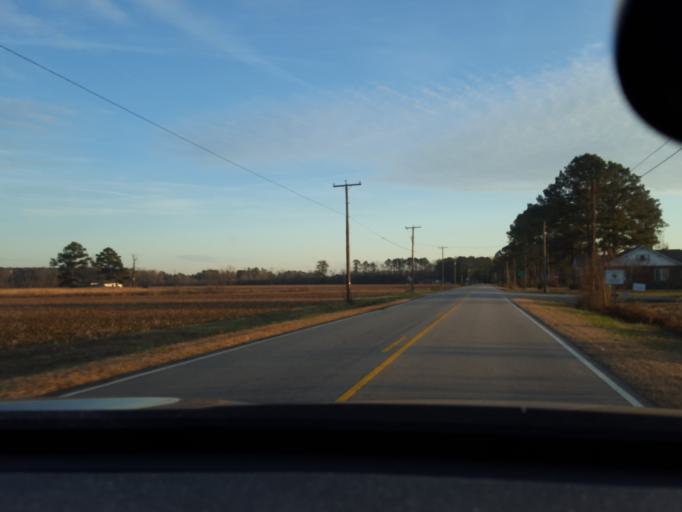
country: US
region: North Carolina
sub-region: Hertford County
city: Ahoskie
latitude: 36.2434
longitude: -77.1185
